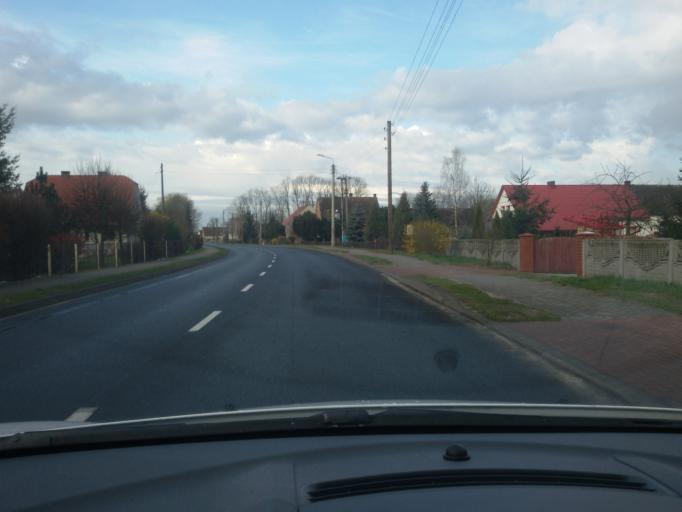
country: PL
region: Lubusz
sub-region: Powiat wschowski
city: Szlichtyngowa
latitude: 51.7243
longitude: 16.2554
